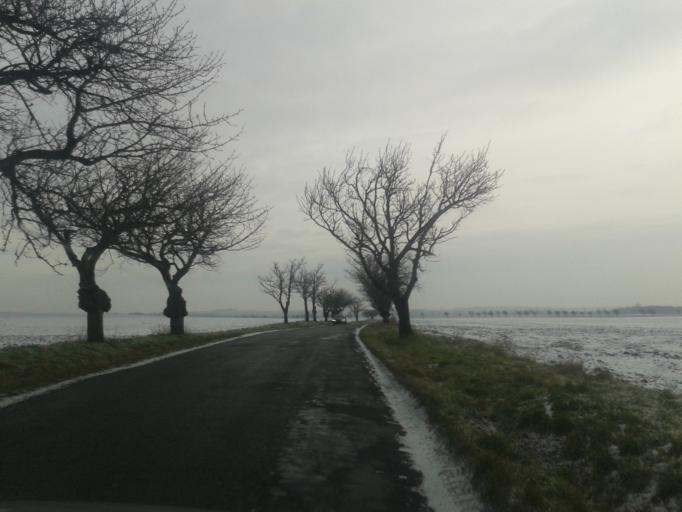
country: CZ
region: Olomoucky
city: Mostkovice
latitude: 49.4801
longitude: 17.0604
